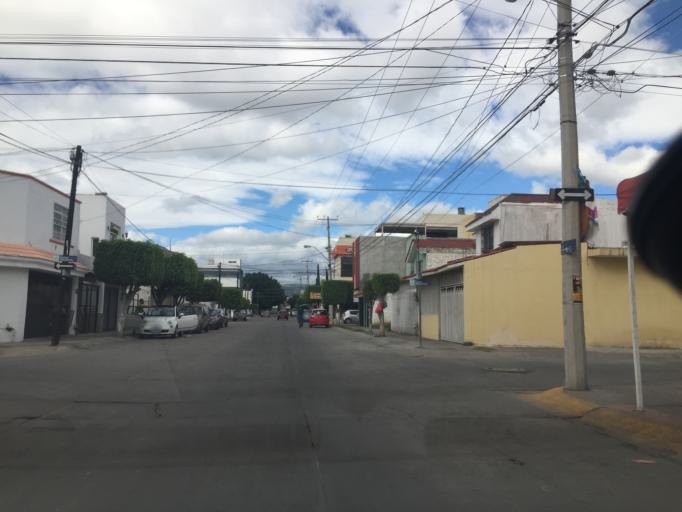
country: MX
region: Guanajuato
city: Leon
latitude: 21.1489
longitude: -101.6574
